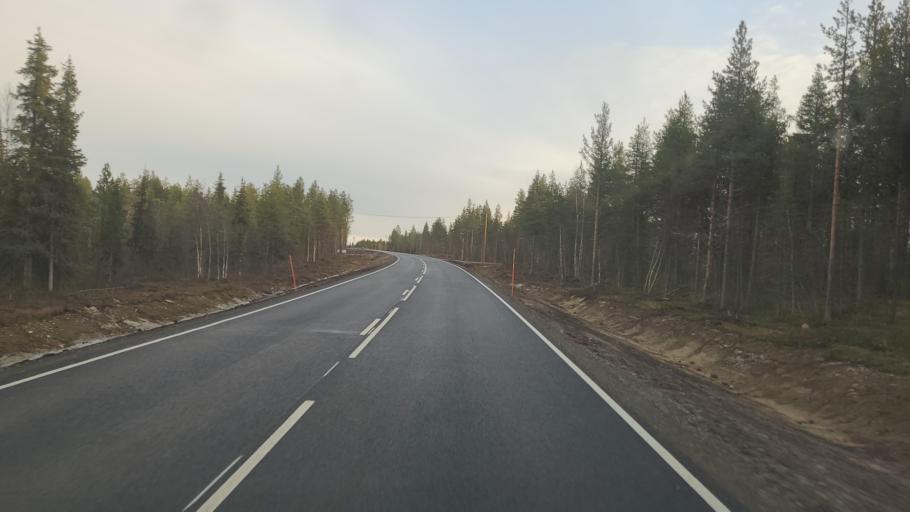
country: FI
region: Lapland
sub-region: Tunturi-Lappi
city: Kittilae
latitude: 67.8723
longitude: 24.8988
